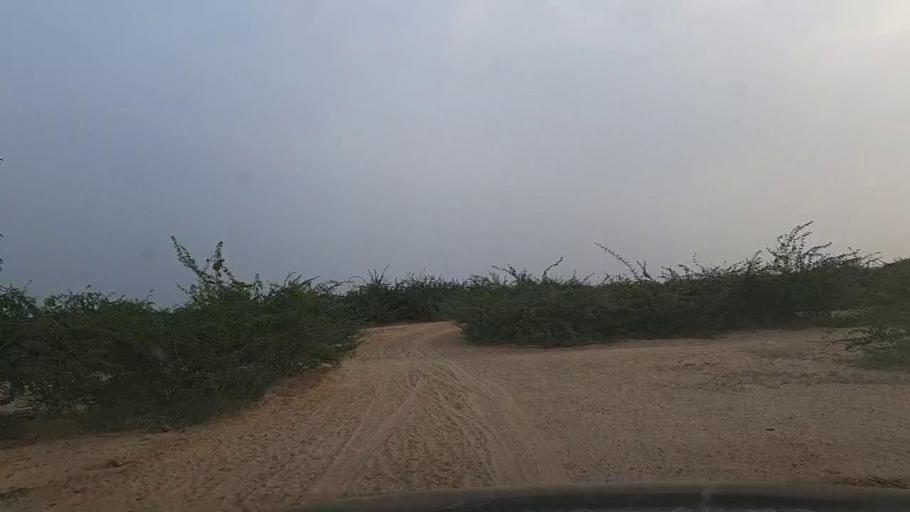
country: PK
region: Sindh
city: Gharo
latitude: 24.7741
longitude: 67.6953
